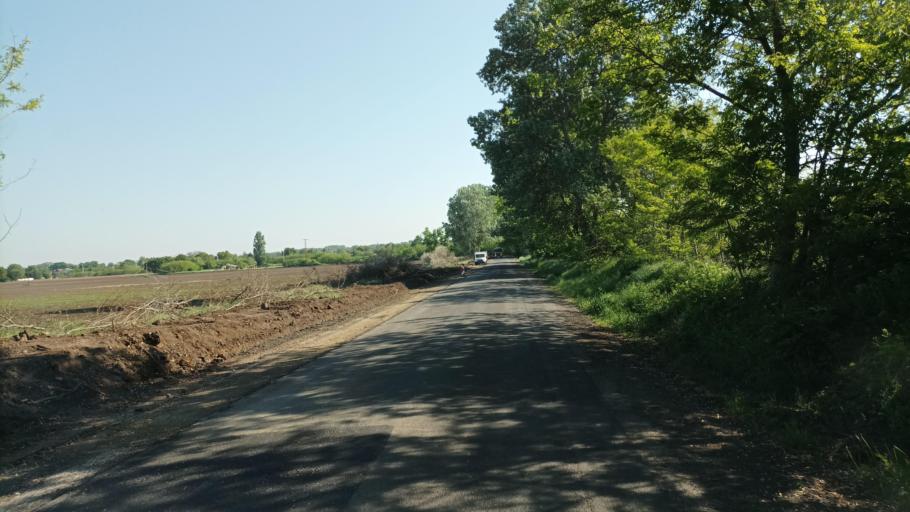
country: HU
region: Pest
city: Nyaregyhaza
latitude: 47.3002
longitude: 19.5013
